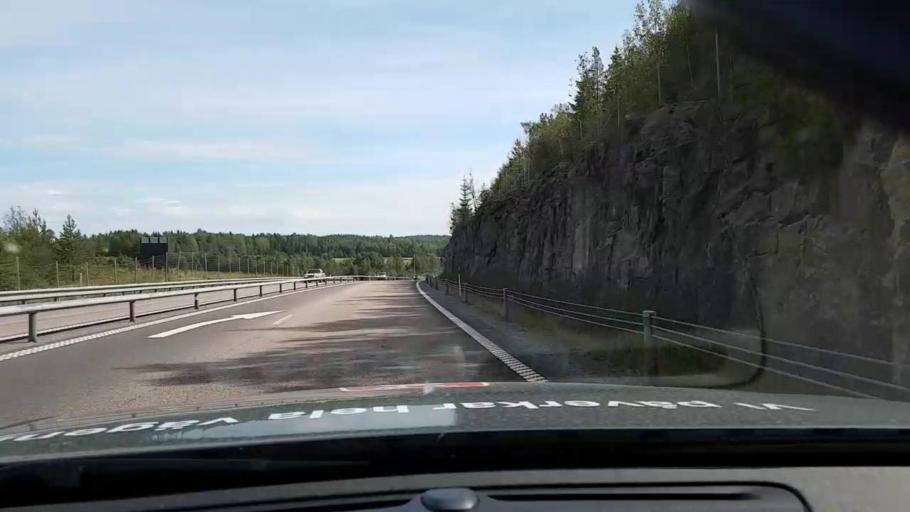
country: SE
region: Vaesternorrland
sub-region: OErnskoeldsviks Kommun
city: Ornskoldsvik
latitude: 63.3105
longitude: 18.8346
